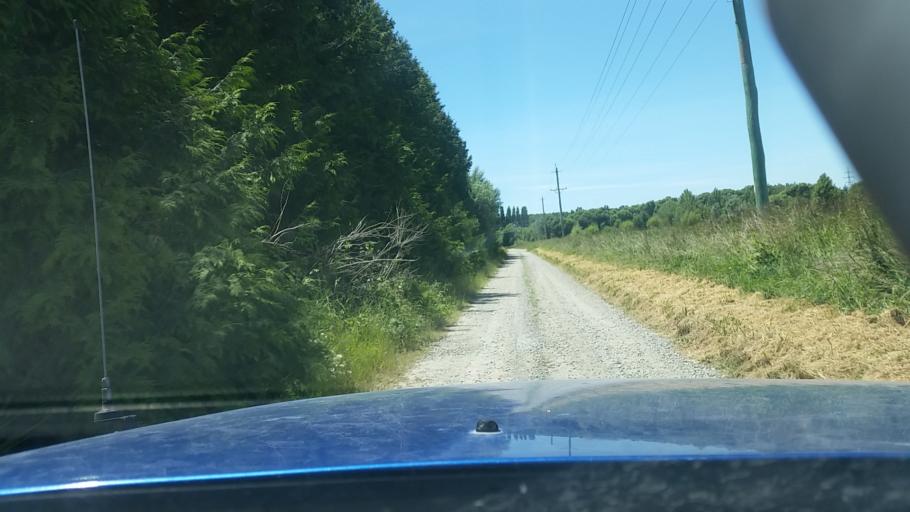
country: NZ
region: Canterbury
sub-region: Ashburton District
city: Tinwald
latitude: -43.9458
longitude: 171.7720
